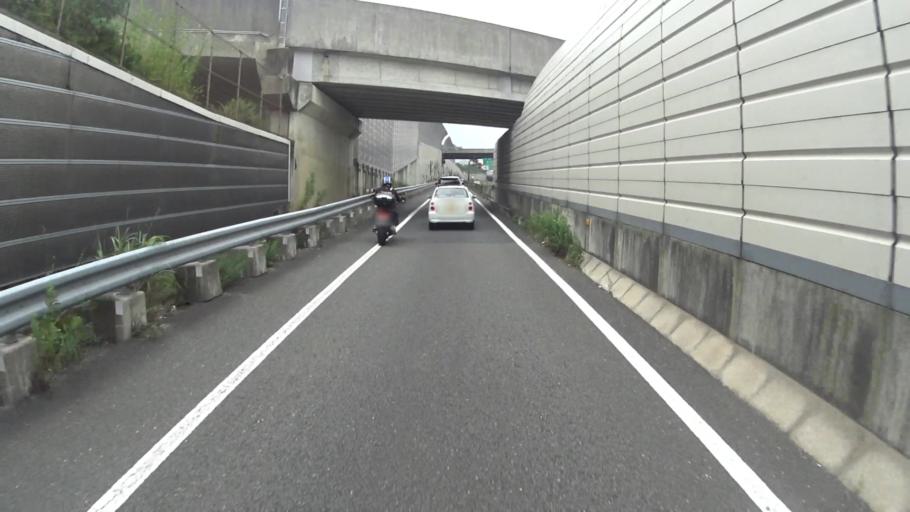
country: JP
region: Kyoto
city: Tanabe
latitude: 34.8292
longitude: 135.7239
